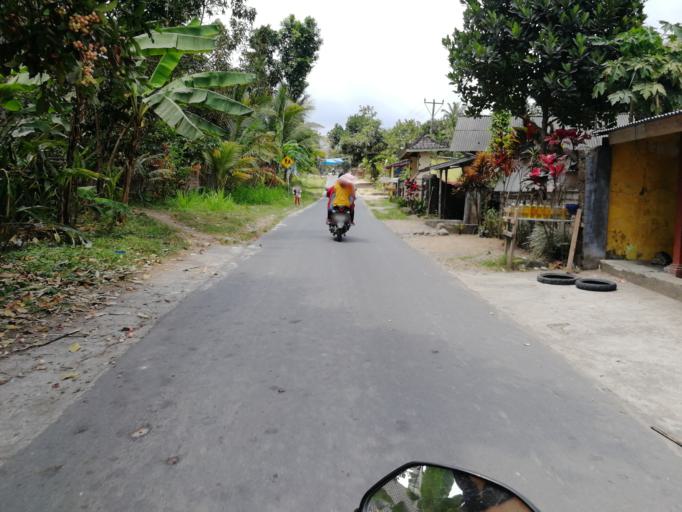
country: ID
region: West Nusa Tenggara
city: Pediti
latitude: -8.5626
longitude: 116.3316
